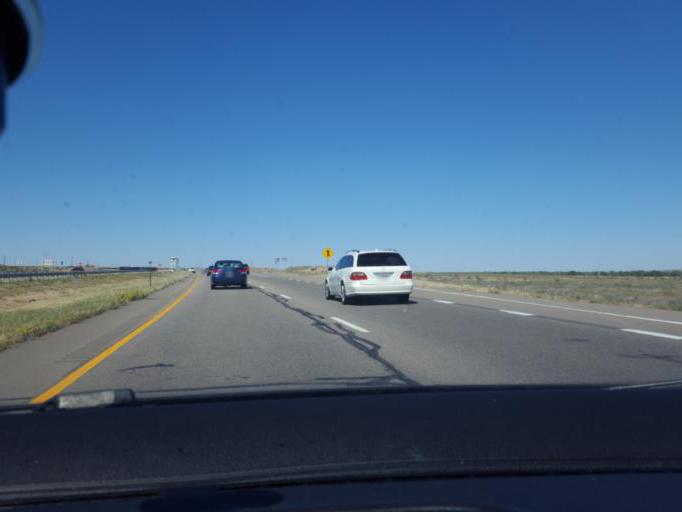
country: US
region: Colorado
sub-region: Pueblo County
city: Pueblo West
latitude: 38.3821
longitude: -104.6187
